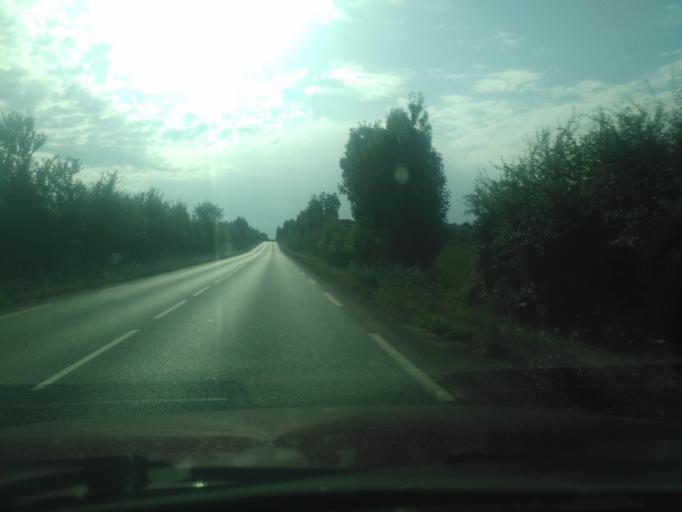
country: FR
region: Pays de la Loire
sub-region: Departement de la Vendee
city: Saint-Germain-de-Princay
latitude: 46.6826
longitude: -1.0092
